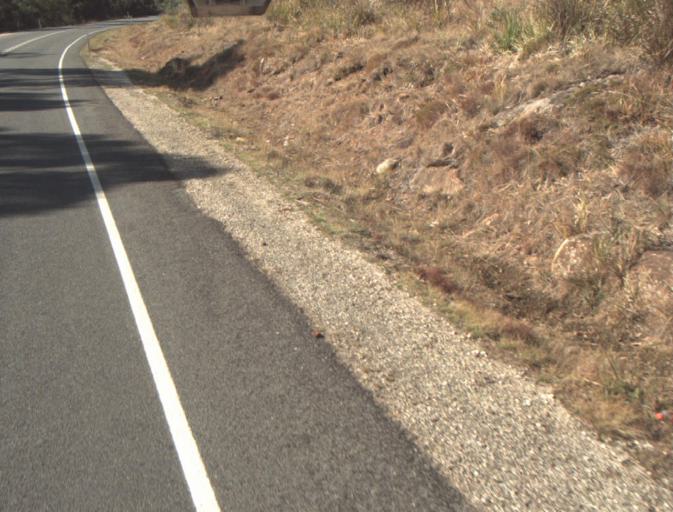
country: AU
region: Tasmania
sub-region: Launceston
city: Mayfield
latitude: -41.3381
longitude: 147.1456
